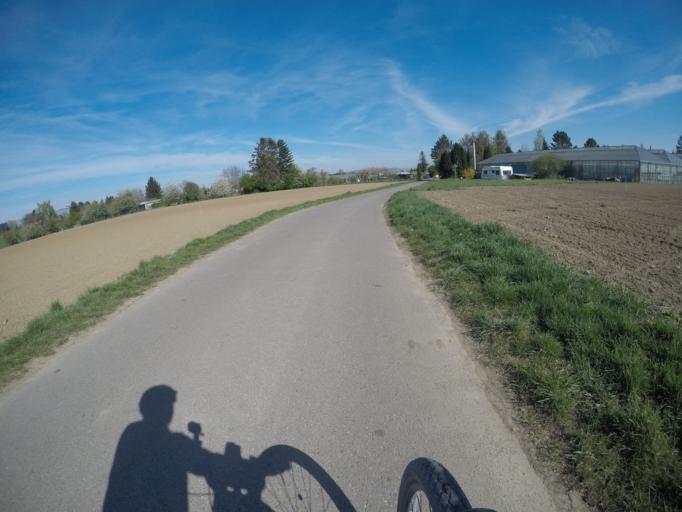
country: DE
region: Baden-Wuerttemberg
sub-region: Regierungsbezirk Stuttgart
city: Kornwestheim
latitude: 48.8684
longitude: 9.1713
